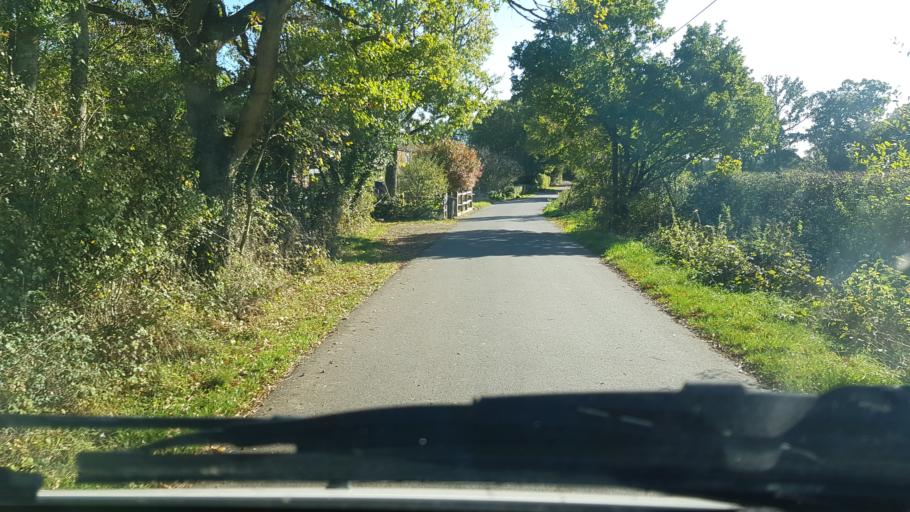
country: GB
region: England
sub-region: Surrey
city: Ockley
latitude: 51.1256
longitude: -0.3612
